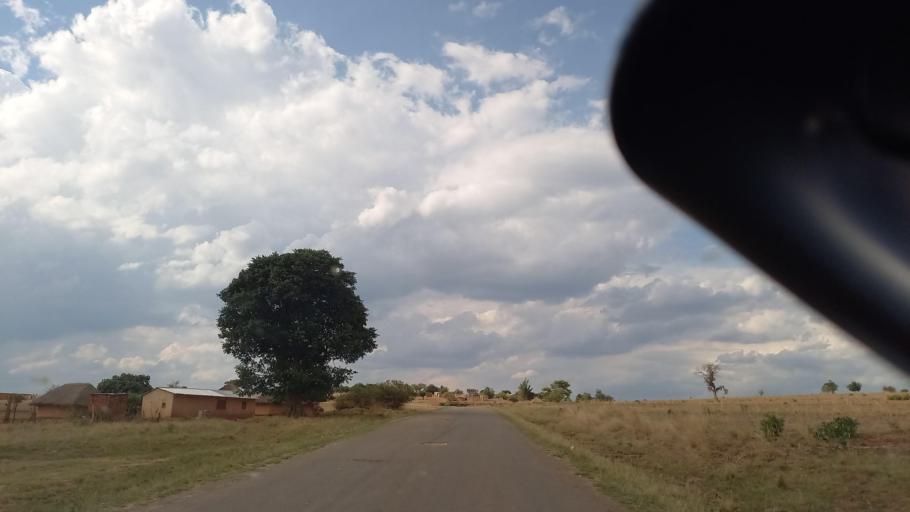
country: ZM
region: Lusaka
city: Kafue
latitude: -16.2068
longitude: 28.1111
